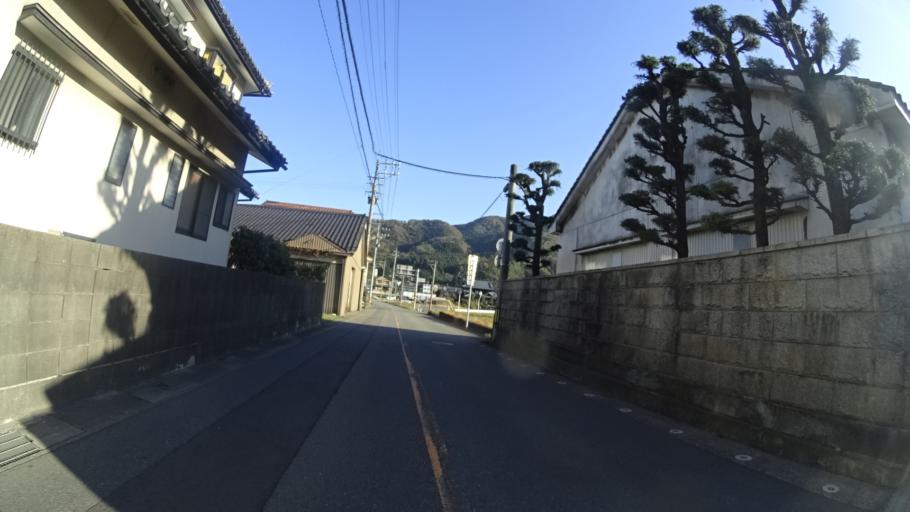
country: JP
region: Fukui
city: Maruoka
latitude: 36.0999
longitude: 136.3263
